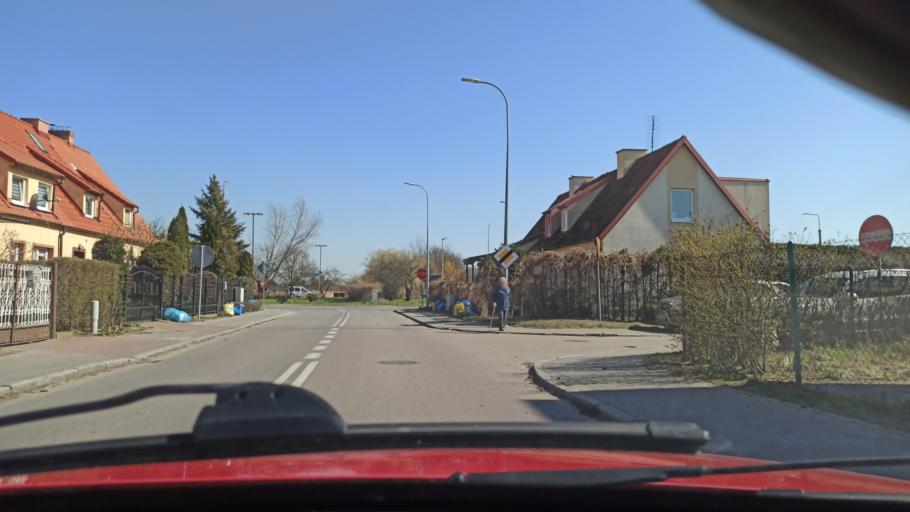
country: PL
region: Warmian-Masurian Voivodeship
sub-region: Powiat elblaski
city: Elblag
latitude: 54.1447
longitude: 19.4084
